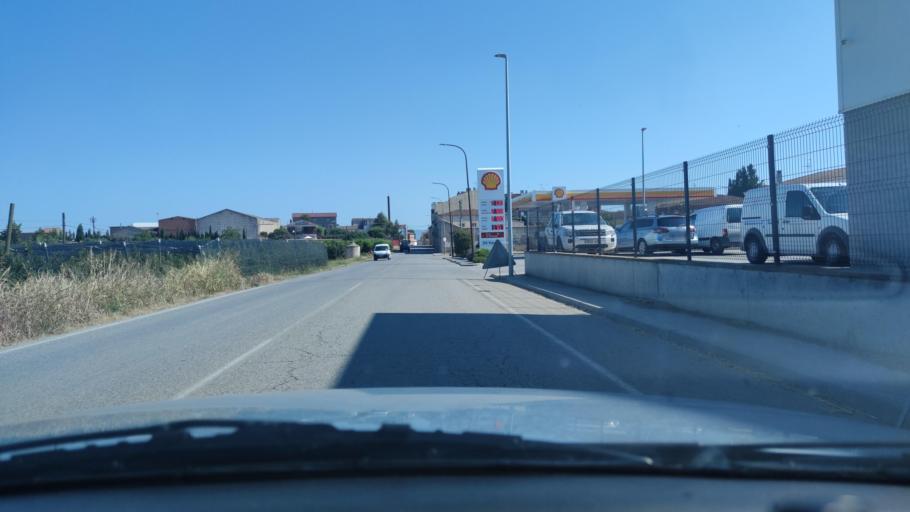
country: ES
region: Catalonia
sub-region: Provincia de Lleida
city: Bellvis
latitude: 41.6697
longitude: 0.8141
